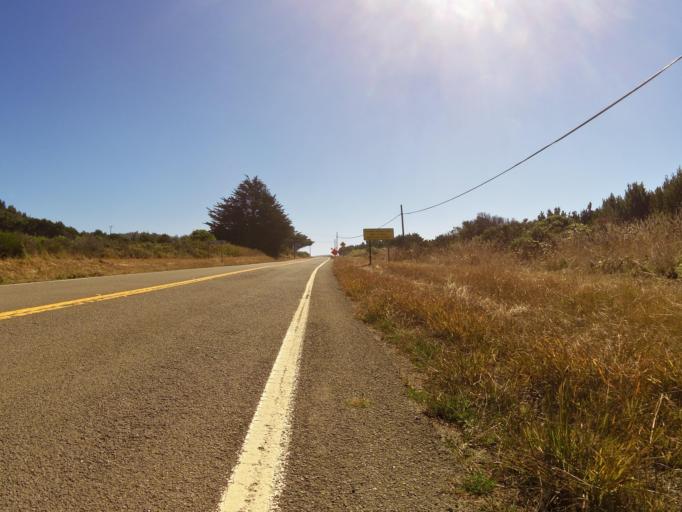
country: US
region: California
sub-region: Mendocino County
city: Fort Bragg
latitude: 39.6557
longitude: -123.7845
